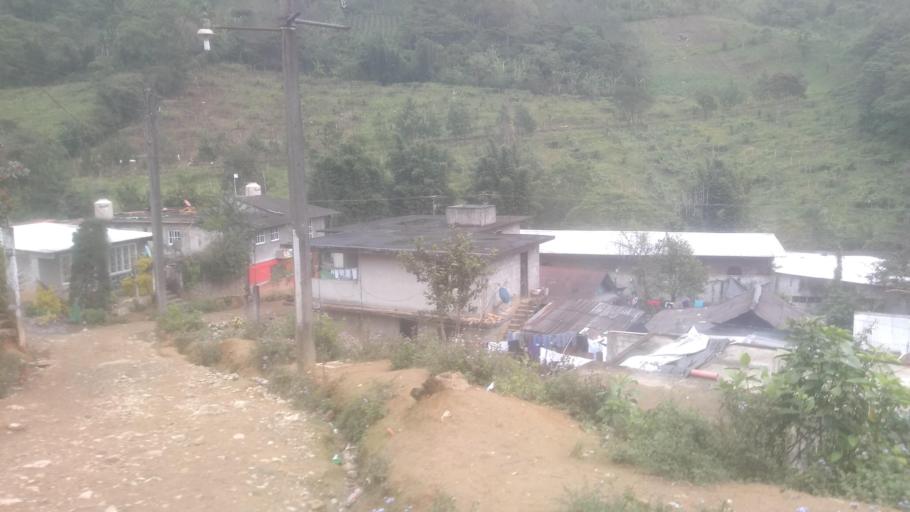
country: MX
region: Veracruz
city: Chocaman
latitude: 18.9953
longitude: -97.0584
